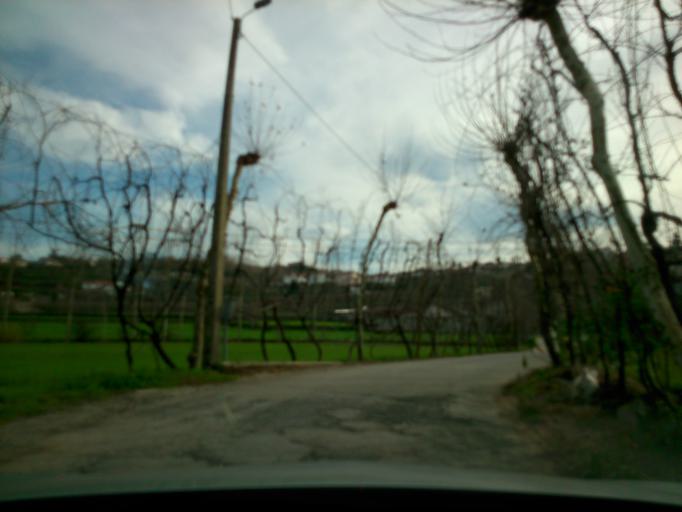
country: PT
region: Porto
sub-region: Amarante
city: Figueiro
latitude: 41.2970
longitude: -8.2174
